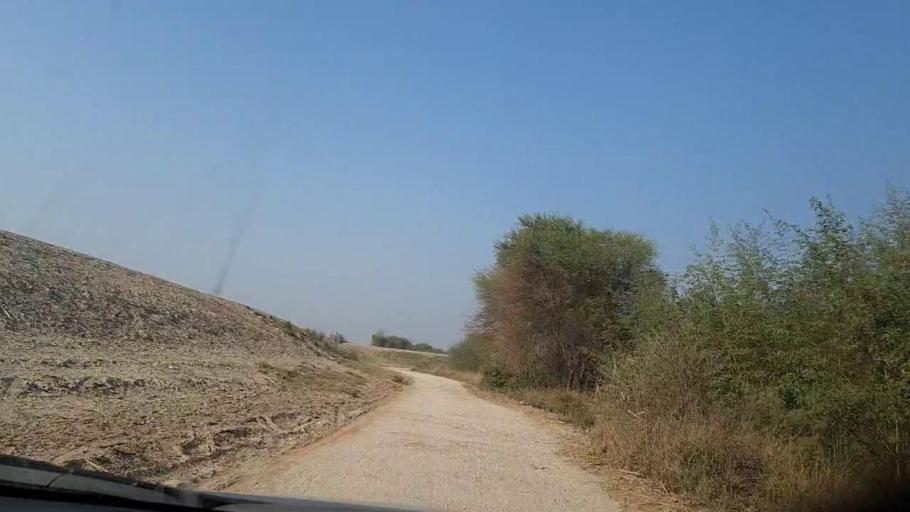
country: PK
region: Sindh
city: Moro
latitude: 26.8120
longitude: 67.9553
